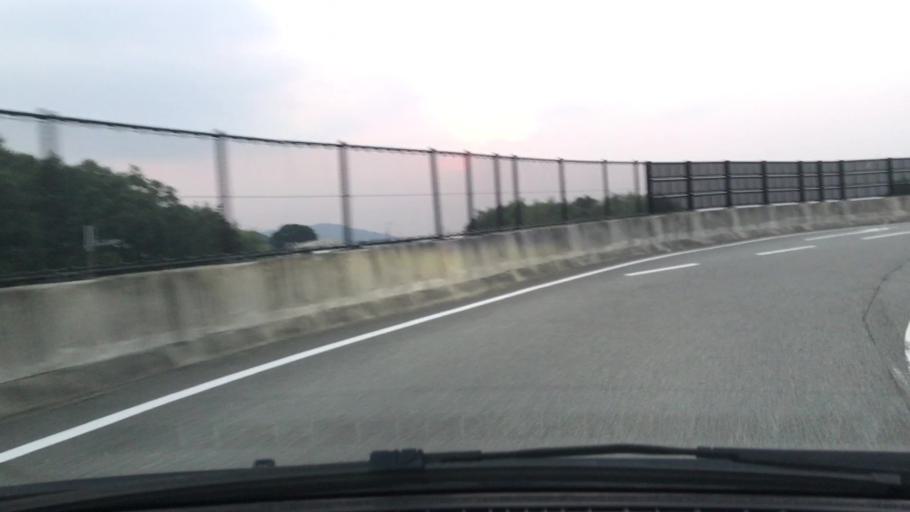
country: JP
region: Hyogo
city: Takarazuka
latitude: 34.8309
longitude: 135.2909
